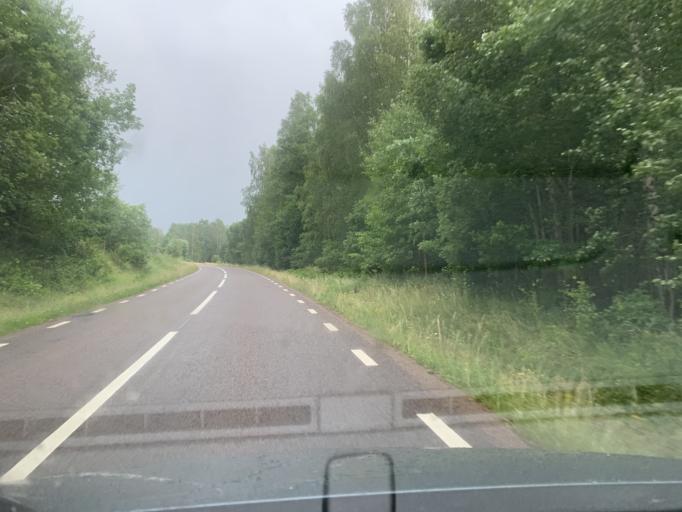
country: SE
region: Kalmar
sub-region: Vasterviks Kommun
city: Overum
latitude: 58.0100
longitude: 16.1727
